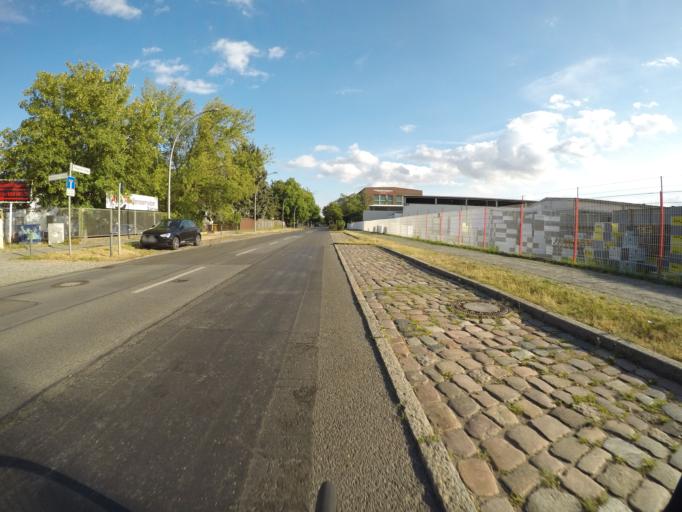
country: DE
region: Berlin
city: Weissensee
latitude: 52.5645
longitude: 13.4767
